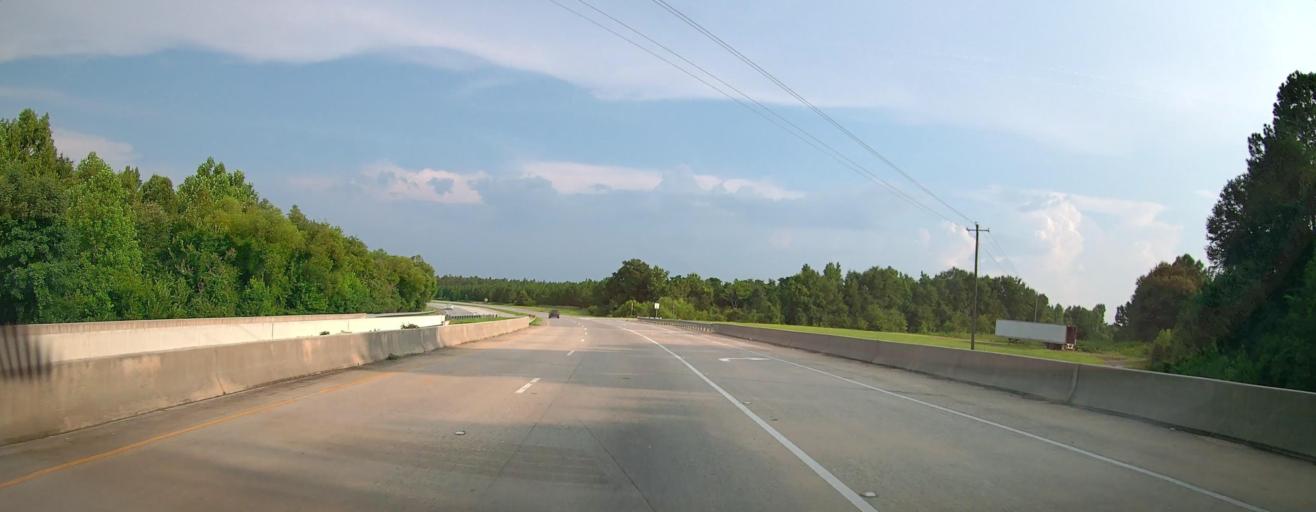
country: US
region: Georgia
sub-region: Laurens County
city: Dublin
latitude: 32.5471
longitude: -82.9786
